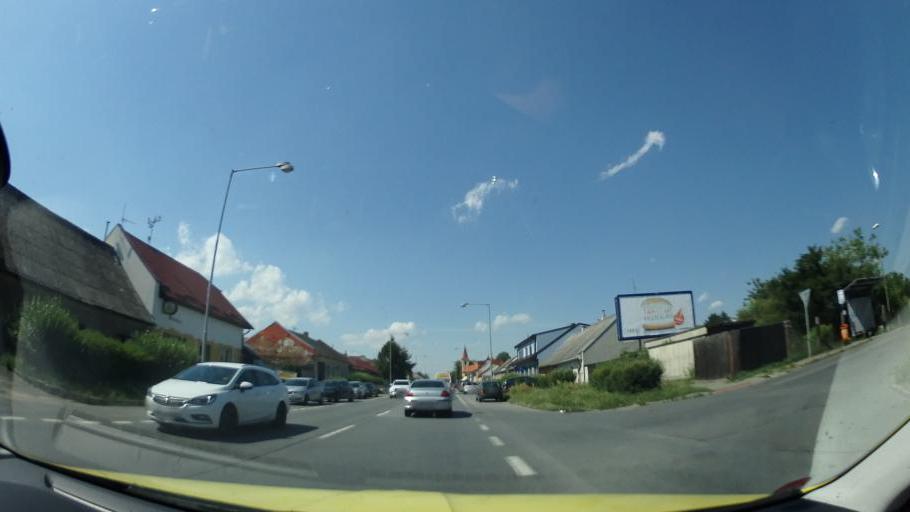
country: CZ
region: Olomoucky
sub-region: Okres Olomouc
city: Olomouc
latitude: 49.5657
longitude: 17.2622
